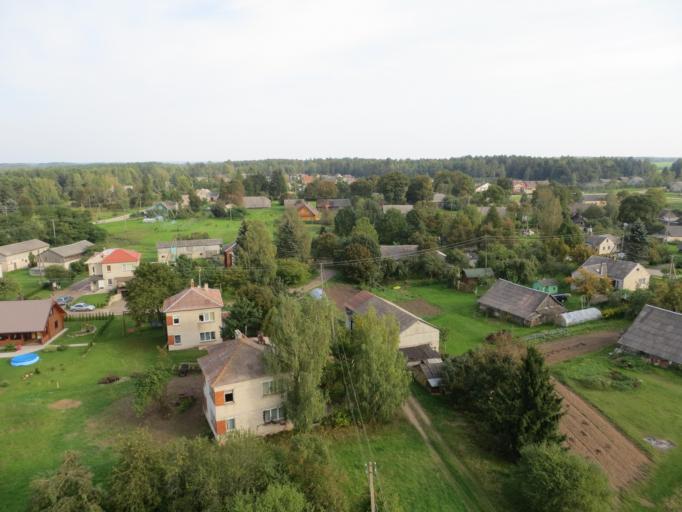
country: LT
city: Moletai
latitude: 55.2725
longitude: 25.5125
